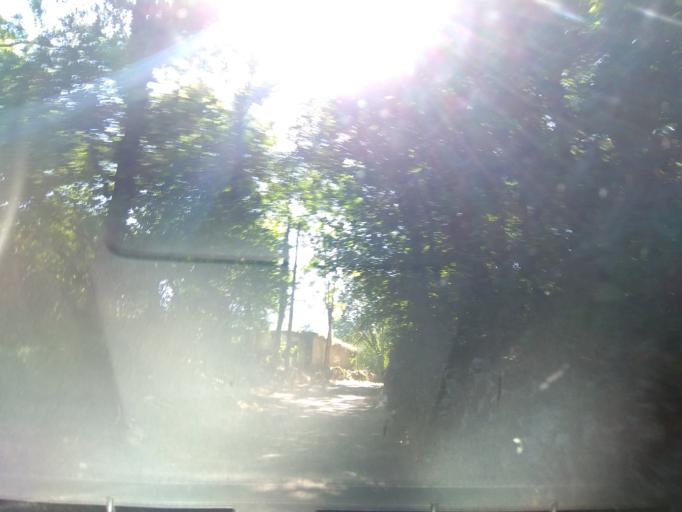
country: ES
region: Catalonia
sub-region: Provincia de Lleida
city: Les
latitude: 42.7539
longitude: 0.6947
